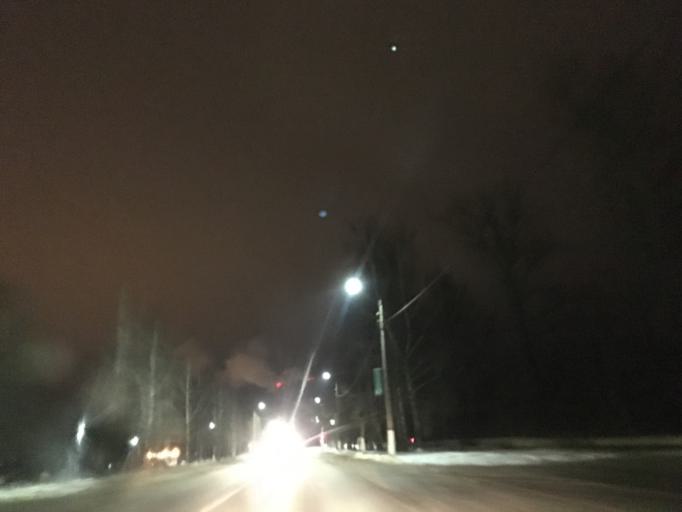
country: RU
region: Tula
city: Pervomayskiy
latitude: 54.0368
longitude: 37.5216
